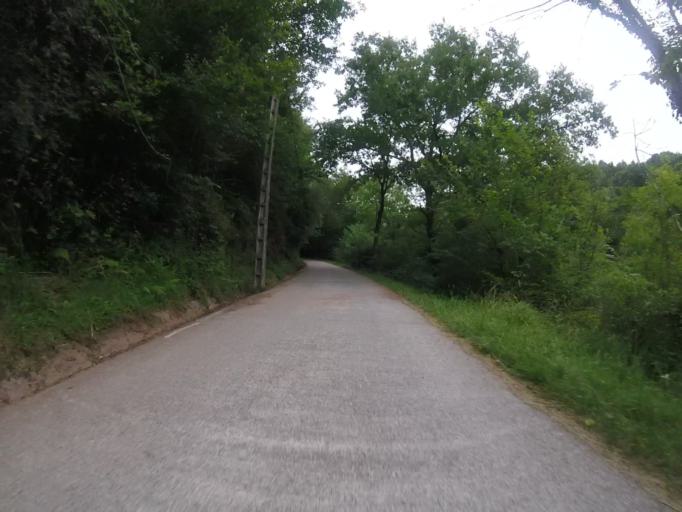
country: ES
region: Navarre
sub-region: Provincia de Navarra
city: Doneztebe
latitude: 43.1472
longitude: -1.6687
